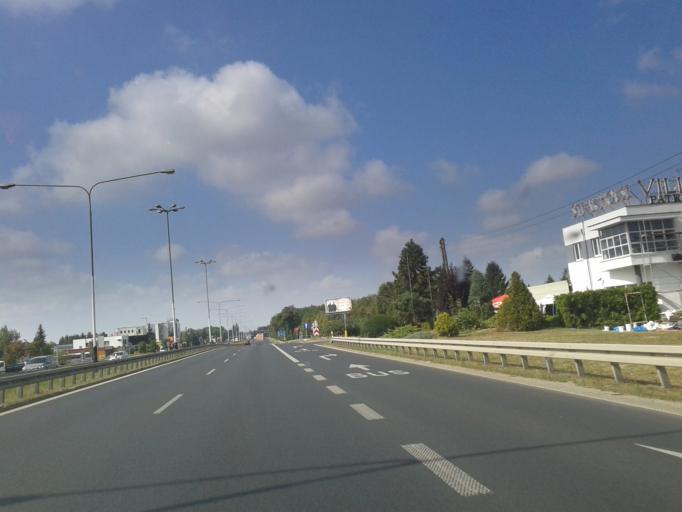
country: PL
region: Greater Poland Voivodeship
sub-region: Powiat poznanski
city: Baranowo
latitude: 52.4337
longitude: 16.7983
